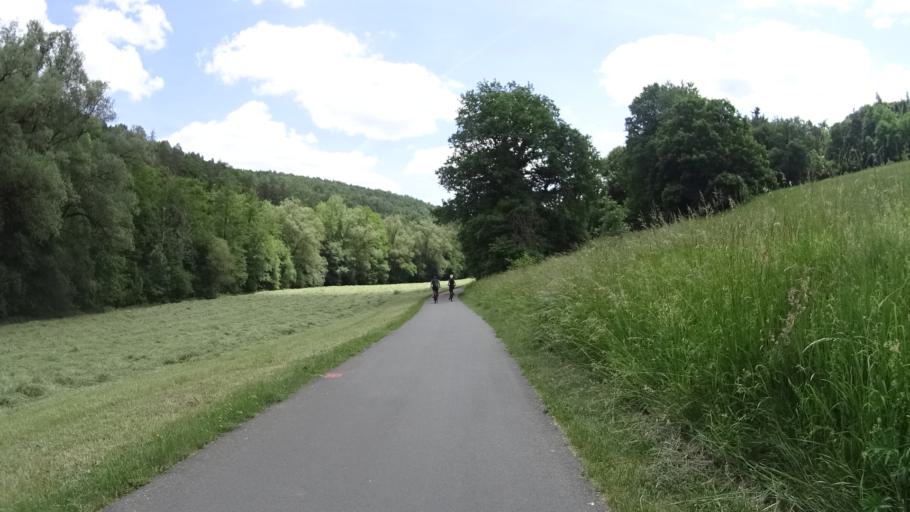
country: DE
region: Bavaria
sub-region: Regierungsbezirk Unterfranken
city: Eichenbuhl
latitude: 49.6886
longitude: 9.3513
